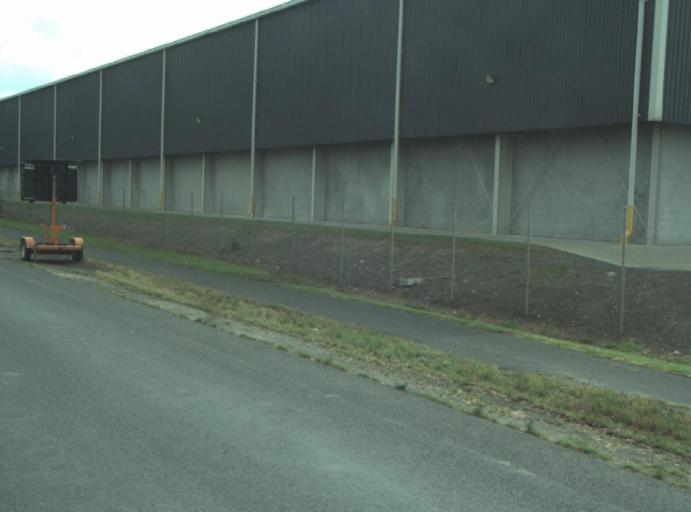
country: AU
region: Victoria
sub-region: Greater Geelong
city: Bell Park
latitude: -38.0855
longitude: 144.3748
